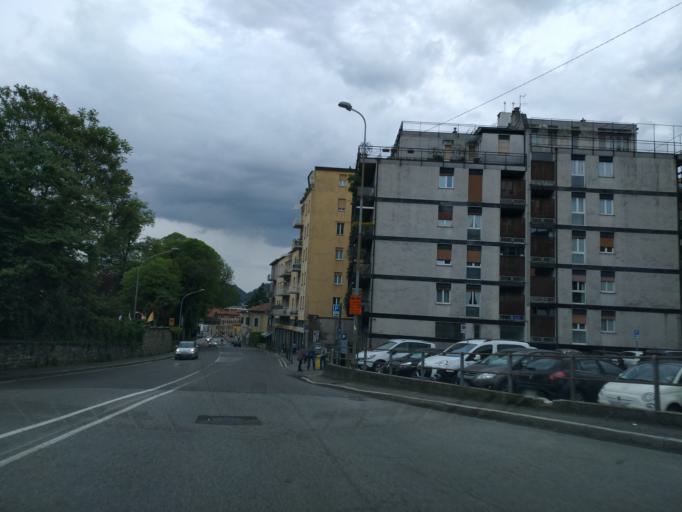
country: IT
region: Lombardy
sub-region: Provincia di Como
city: San Fermo della Battaglia
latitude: 45.8186
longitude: 9.0634
